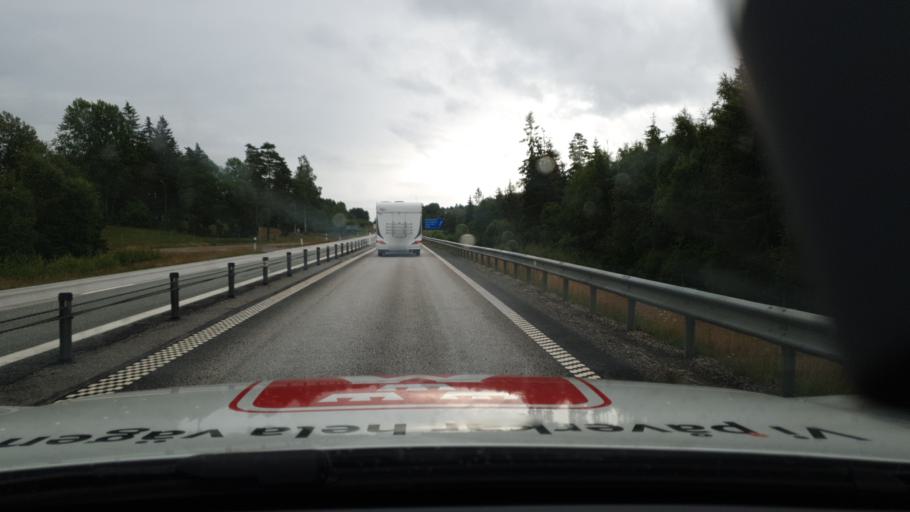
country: SE
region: Joenkoeping
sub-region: Nassjo Kommun
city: Malmback
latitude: 57.6899
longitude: 14.4551
